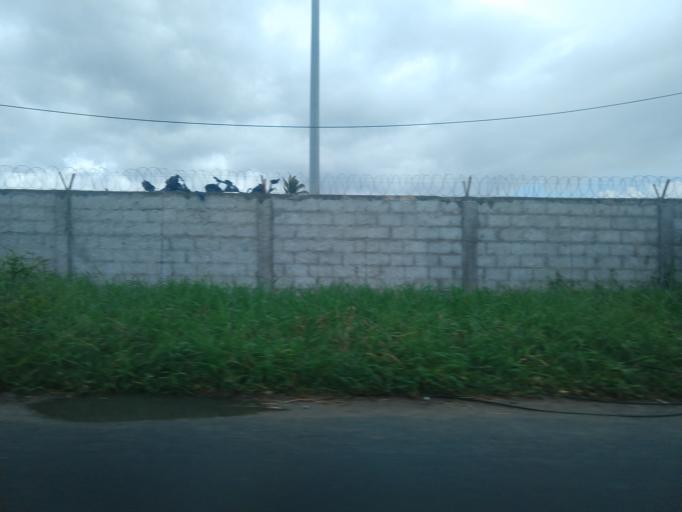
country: MZ
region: Sofala
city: Beira
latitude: -19.7936
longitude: 34.8900
